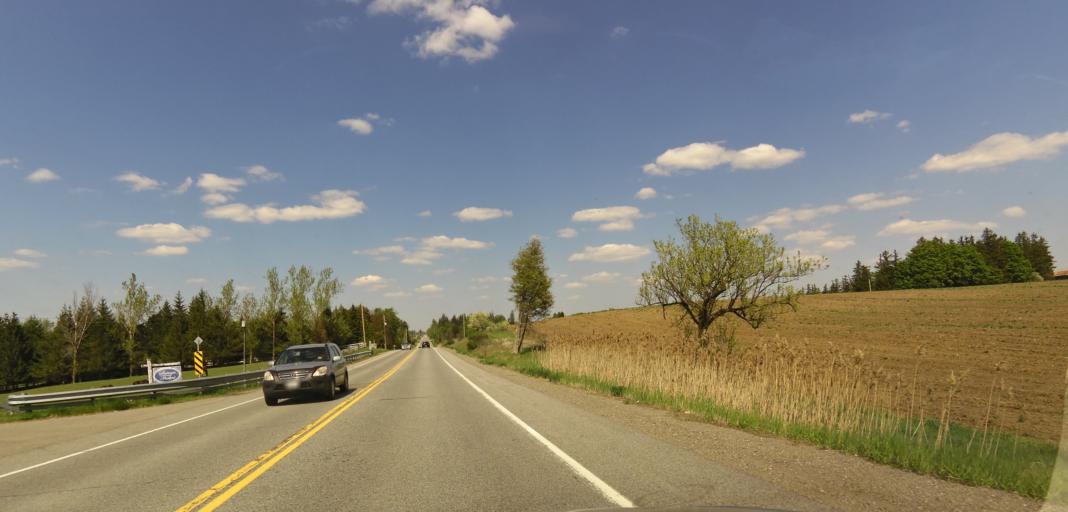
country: CA
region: Ontario
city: Brampton
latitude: 43.8347
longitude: -79.8777
